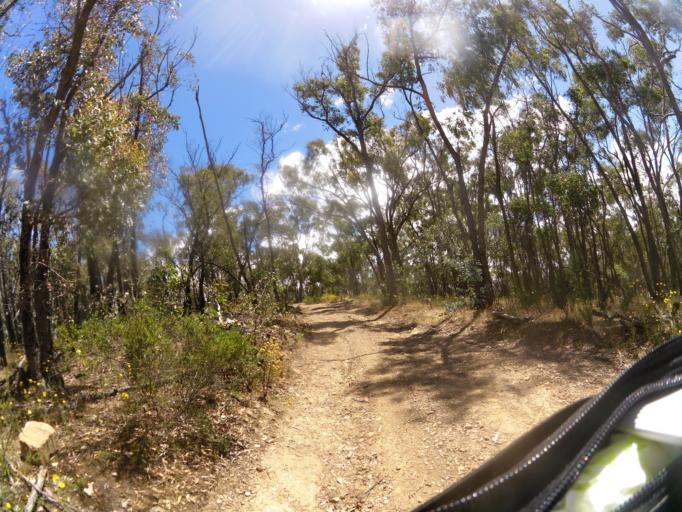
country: AU
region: Victoria
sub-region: Mount Alexander
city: Castlemaine
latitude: -37.0686
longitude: 144.2652
